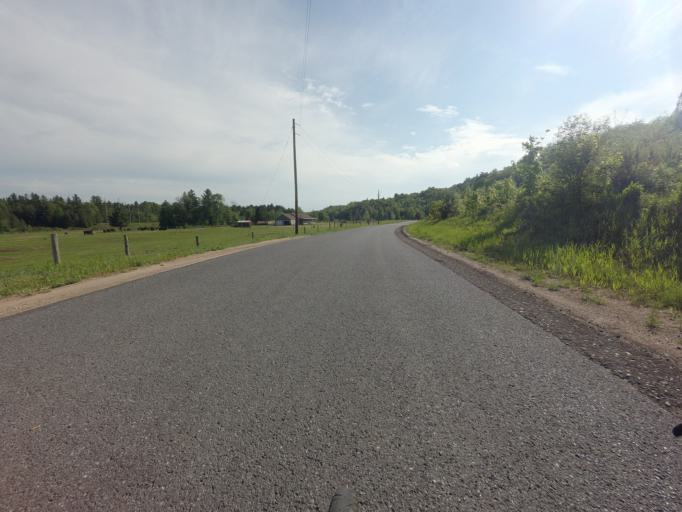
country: US
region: New York
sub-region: St. Lawrence County
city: Gouverneur
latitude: 44.2117
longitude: -75.2441
